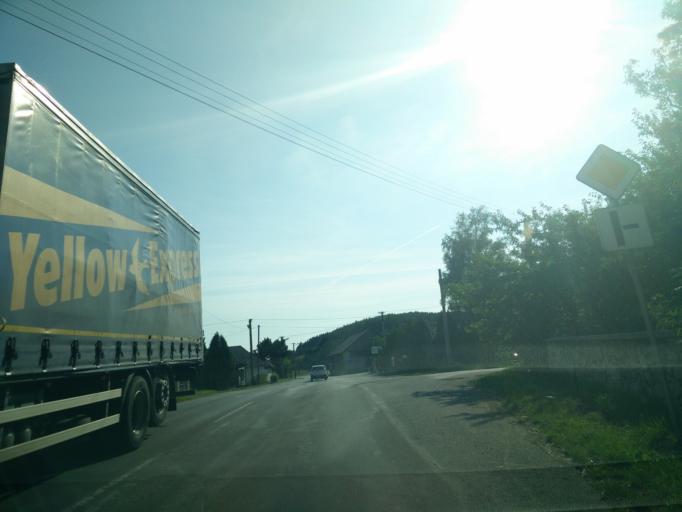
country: SK
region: Zilinsky
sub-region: Okres Martin
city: Martin
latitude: 48.9434
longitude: 18.8302
